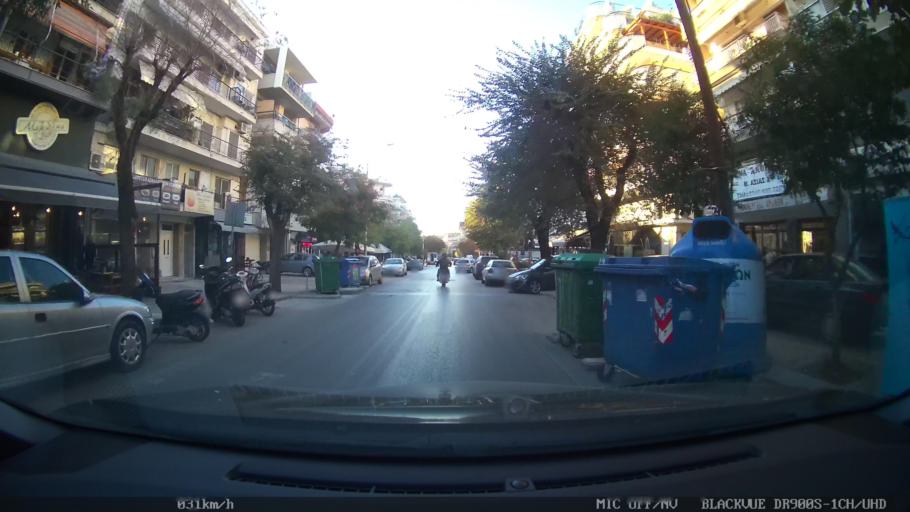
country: GR
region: Central Macedonia
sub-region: Nomos Thessalonikis
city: Triandria
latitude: 40.6123
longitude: 22.9738
